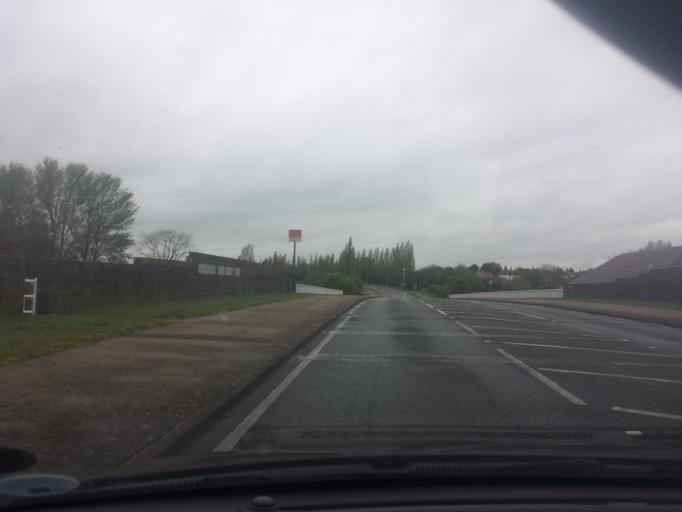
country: GB
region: England
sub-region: Essex
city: Little Clacton
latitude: 51.8530
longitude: 1.1162
